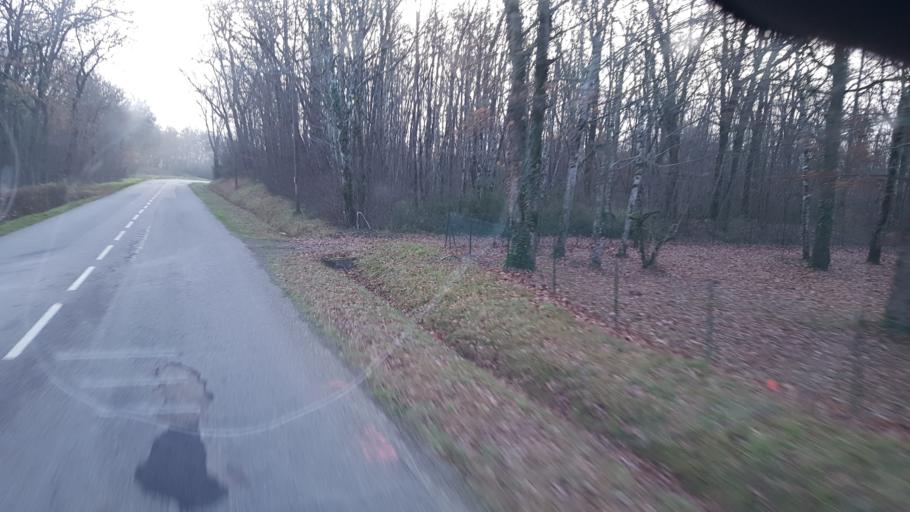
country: FR
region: Midi-Pyrenees
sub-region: Departement du Tarn-et-Garonne
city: Monteils
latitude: 44.1360
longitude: 1.5747
